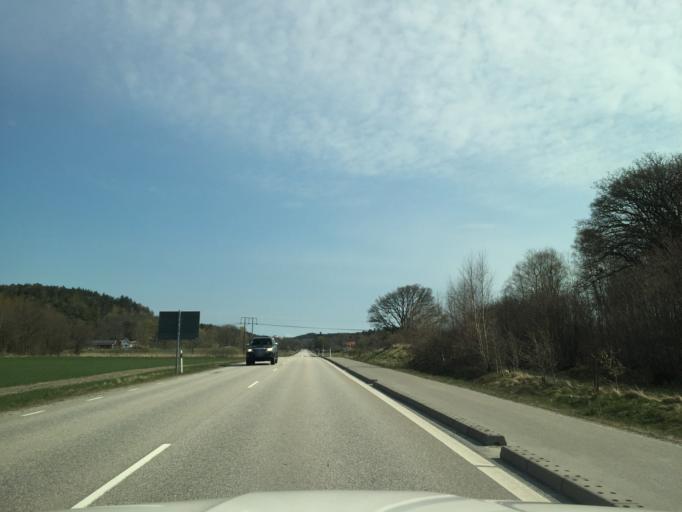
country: SE
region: Vaestra Goetaland
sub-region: Stenungsunds Kommun
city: Stora Hoga
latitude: 58.0320
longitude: 11.8757
